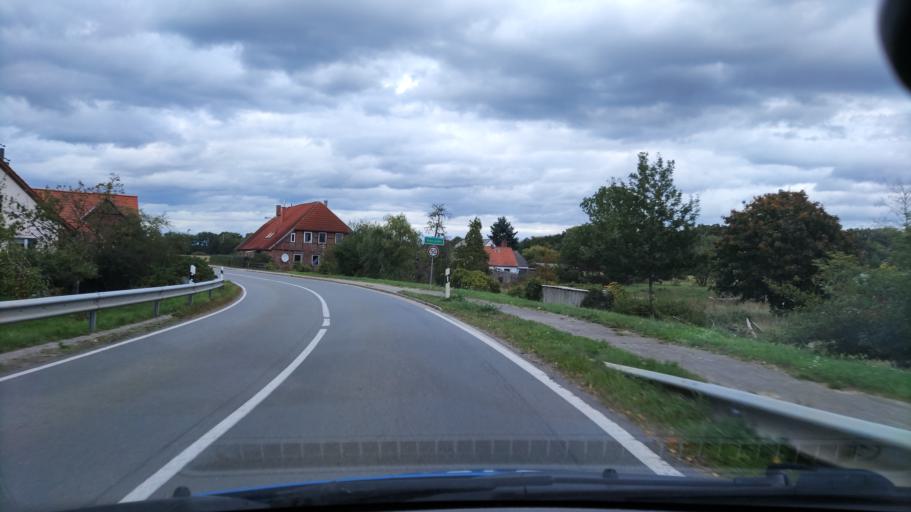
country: DE
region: Lower Saxony
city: Neu Darchau
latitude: 53.3015
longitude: 10.9699
